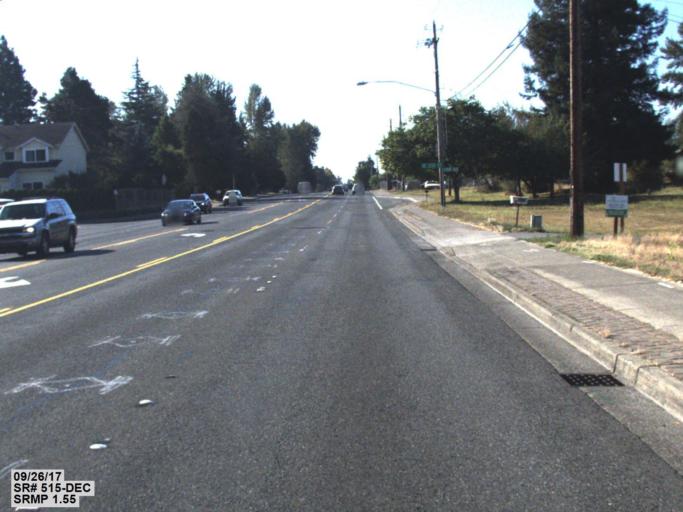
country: US
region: Washington
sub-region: King County
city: East Hill-Meridian
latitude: 47.3950
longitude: -122.2022
